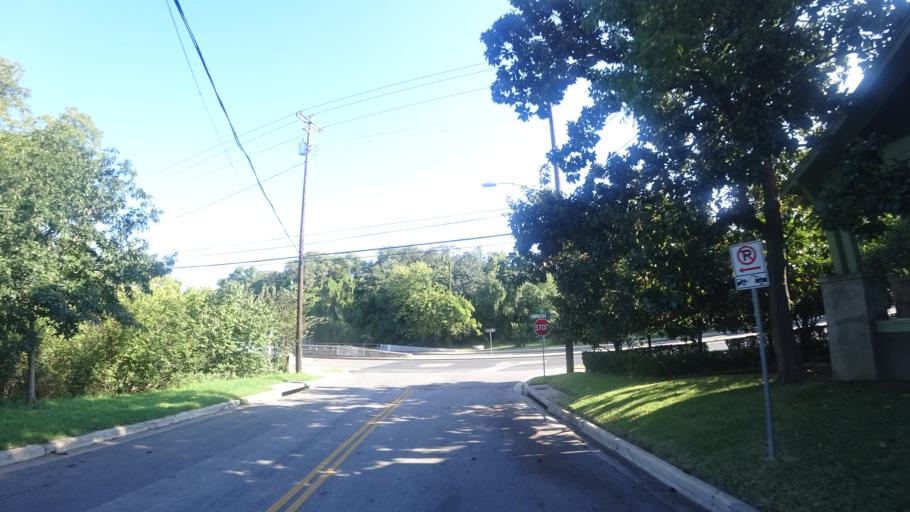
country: US
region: Texas
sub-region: Travis County
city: Austin
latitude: 30.2505
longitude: -97.7407
